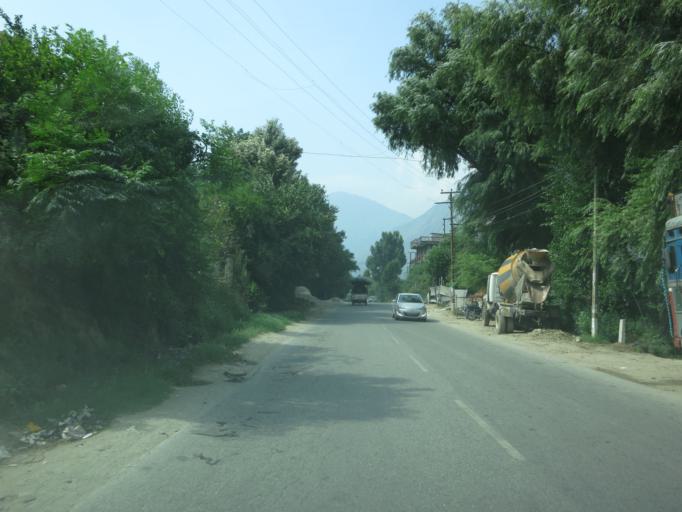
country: IN
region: Himachal Pradesh
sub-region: Kulu
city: Kulu
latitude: 31.8495
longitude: 77.1574
